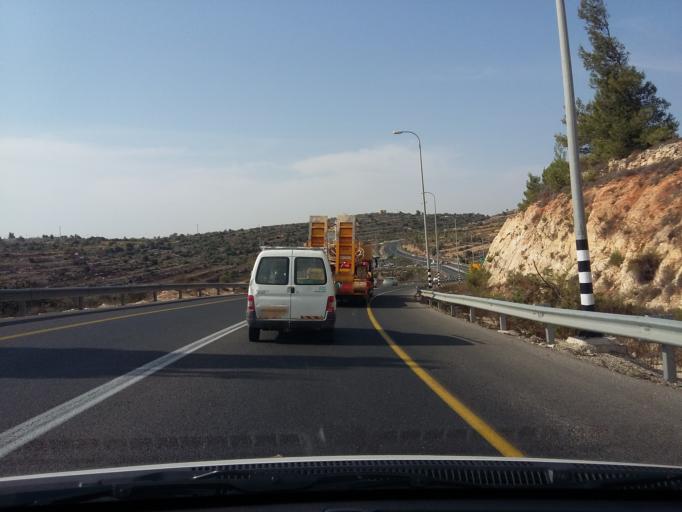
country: PS
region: West Bank
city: Al Khadir
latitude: 31.6893
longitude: 35.1622
